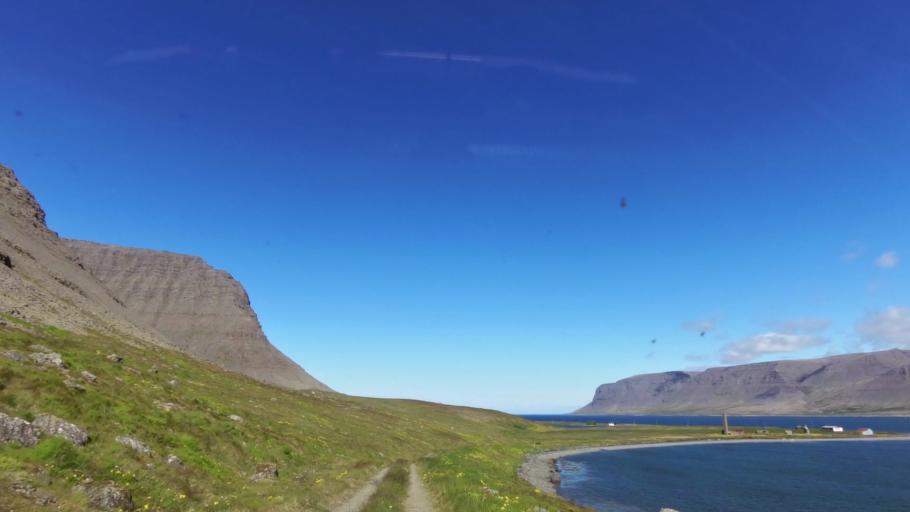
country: IS
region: West
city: Olafsvik
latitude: 65.6356
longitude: -23.9275
